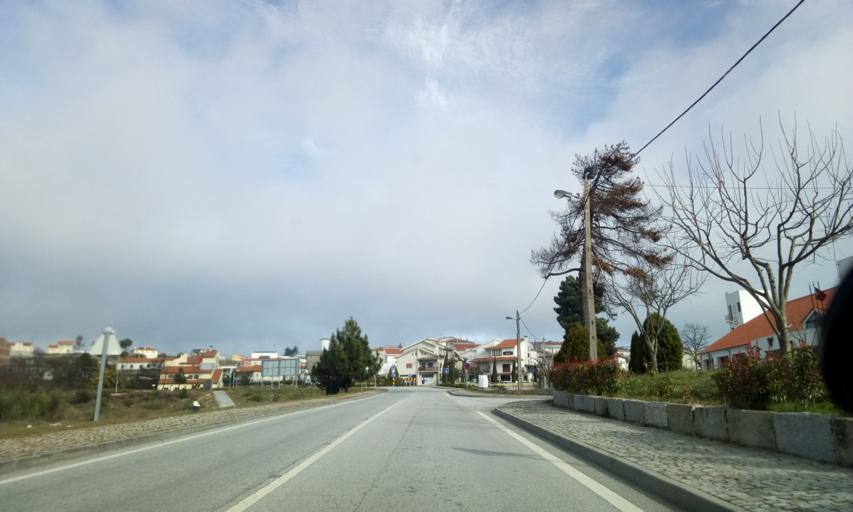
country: PT
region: Guarda
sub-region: Aguiar da Beira
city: Aguiar da Beira
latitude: 40.8168
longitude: -7.5376
